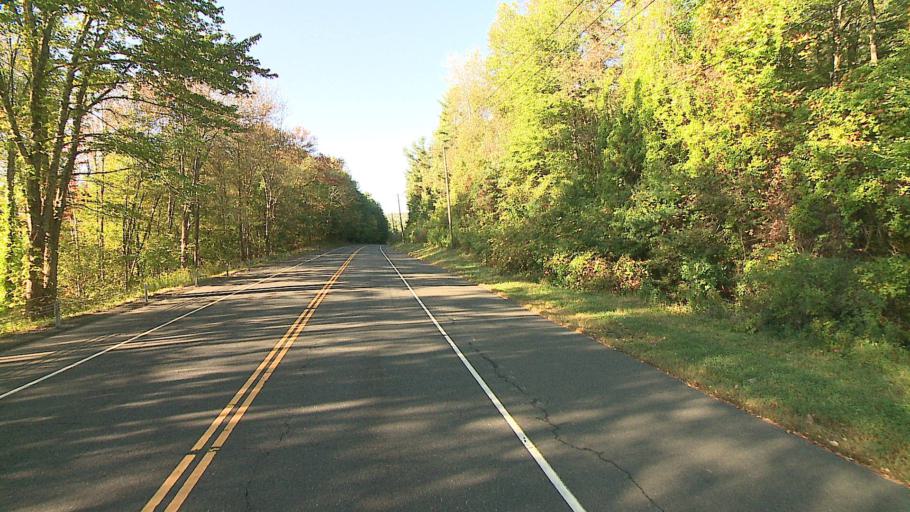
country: US
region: Connecticut
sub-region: Hartford County
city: Collinsville
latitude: 41.8268
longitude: -72.9456
